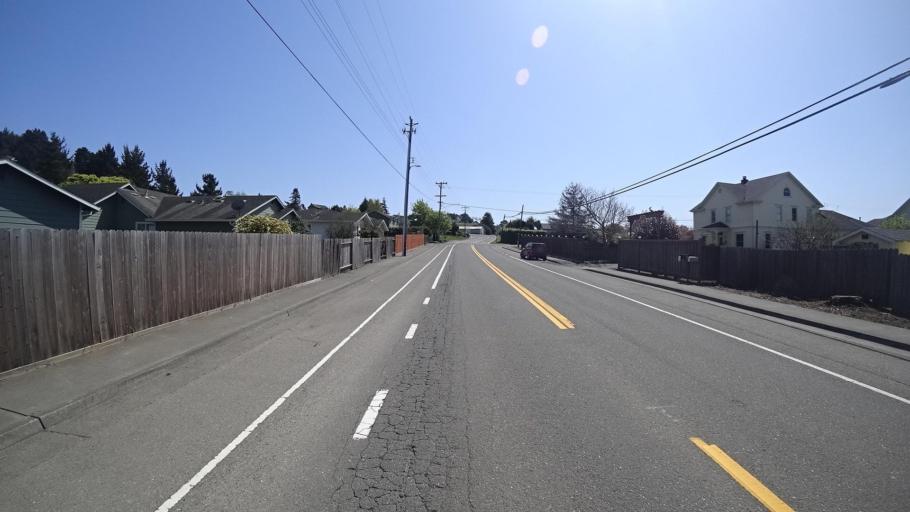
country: US
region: California
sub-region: Humboldt County
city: Hydesville
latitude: 40.5636
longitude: -124.1267
